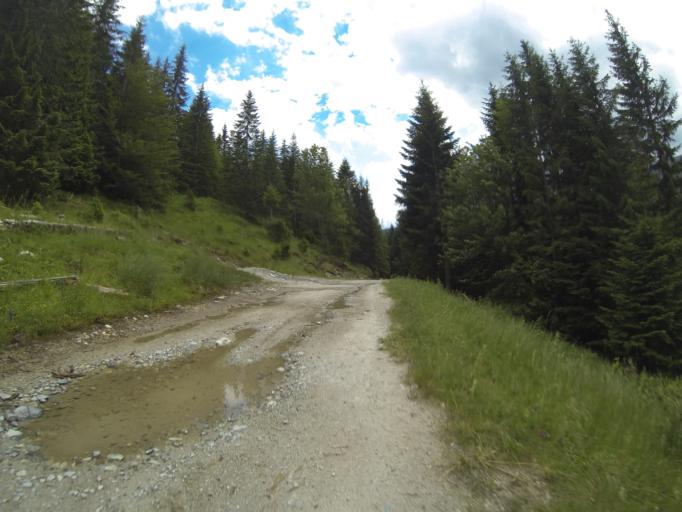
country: RO
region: Gorj
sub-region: Comuna Polovragi
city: Polovragi
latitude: 45.3390
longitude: 23.7949
